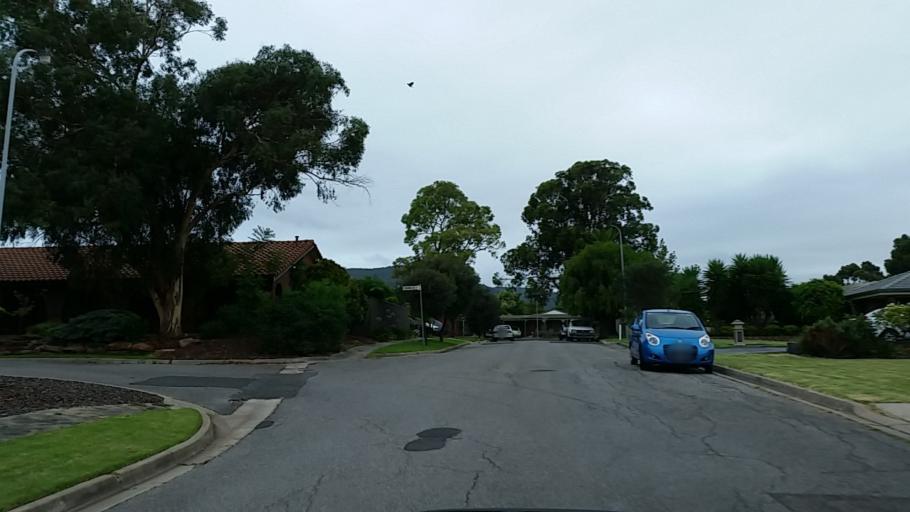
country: AU
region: South Australia
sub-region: Campbelltown
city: Athelstone
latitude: -34.8617
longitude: 138.6975
